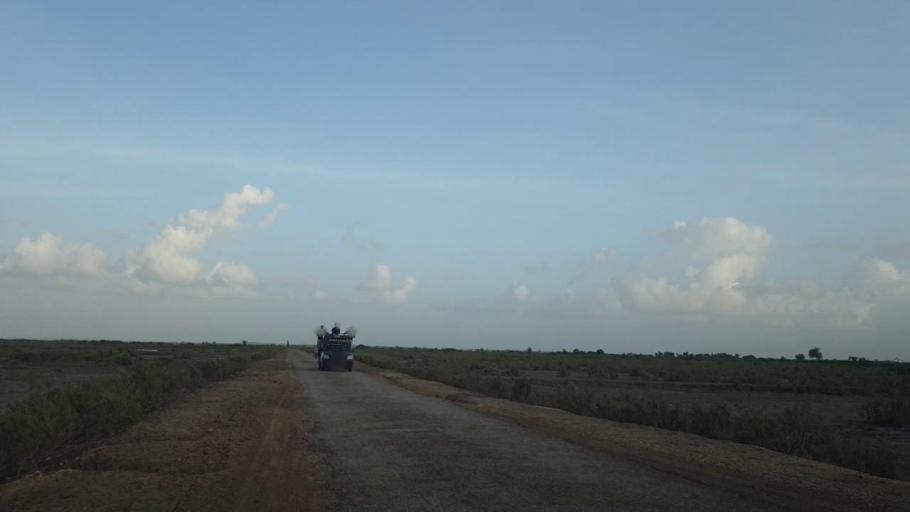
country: PK
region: Sindh
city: Kadhan
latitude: 24.5673
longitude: 69.1193
